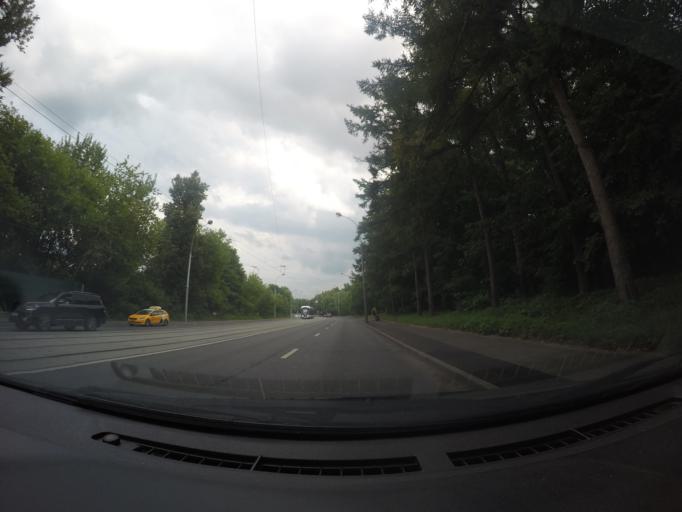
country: RU
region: Moscow
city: Sokol'niki
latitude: 55.8183
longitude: 37.6740
